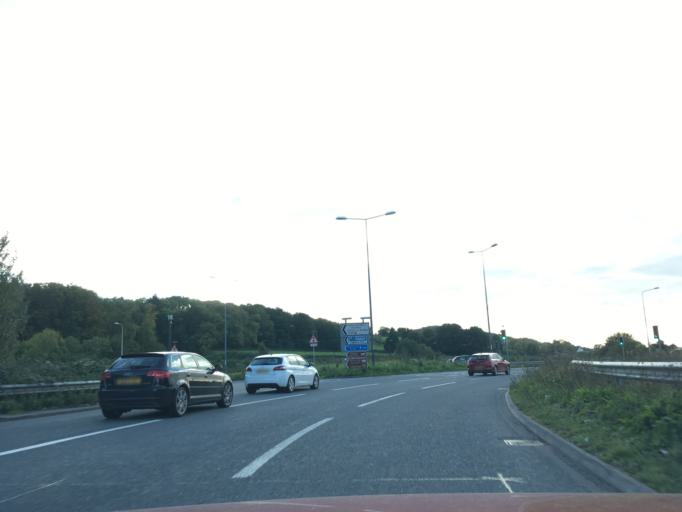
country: GB
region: England
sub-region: North Somerset
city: Easton-in-Gordano
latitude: 51.4763
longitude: -2.7110
